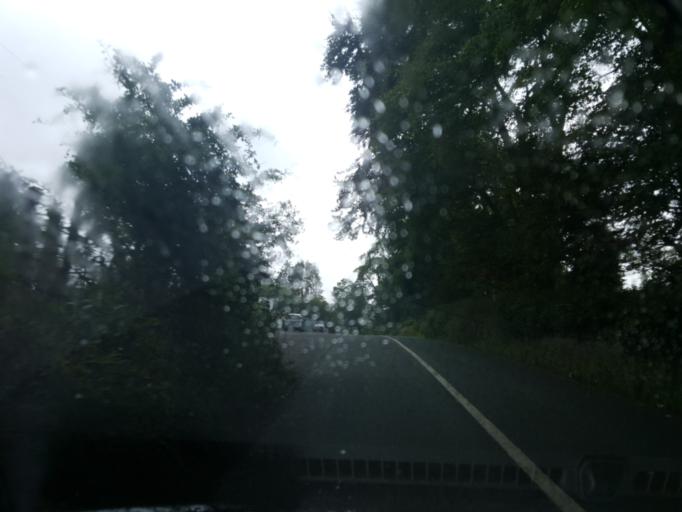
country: IE
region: Leinster
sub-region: Wicklow
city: Valleymount
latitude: 53.1293
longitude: -6.5889
